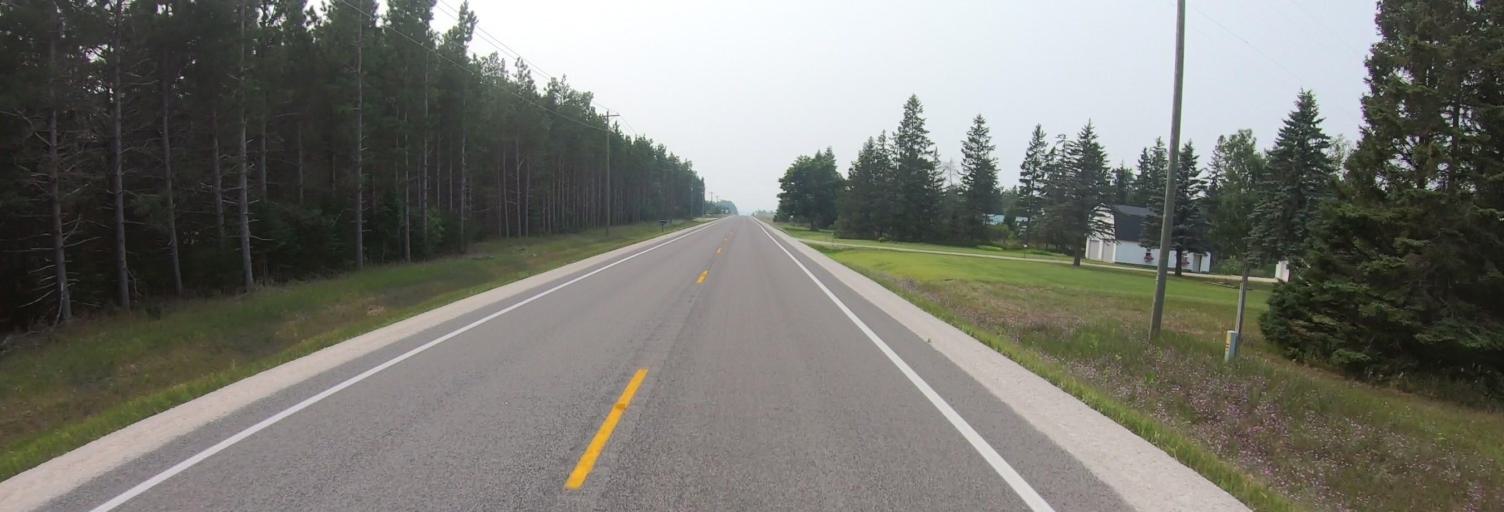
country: US
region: Michigan
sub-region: Chippewa County
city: Sault Ste. Marie
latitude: 46.0722
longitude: -84.1658
